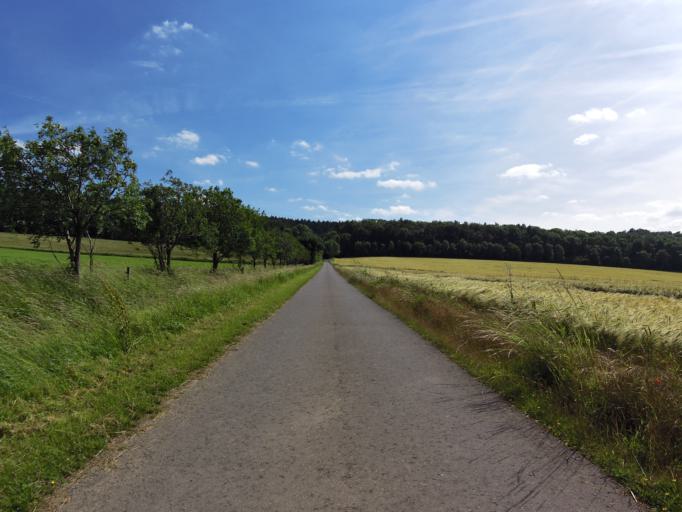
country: DE
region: Thuringia
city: Seebach
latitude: 50.9724
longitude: 10.4330
